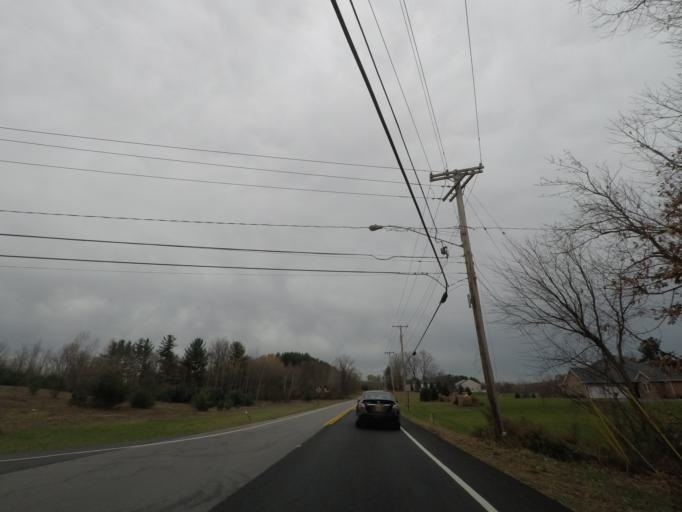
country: US
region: New York
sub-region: Schenectady County
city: Niskayuna
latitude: 42.8322
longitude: -73.8233
